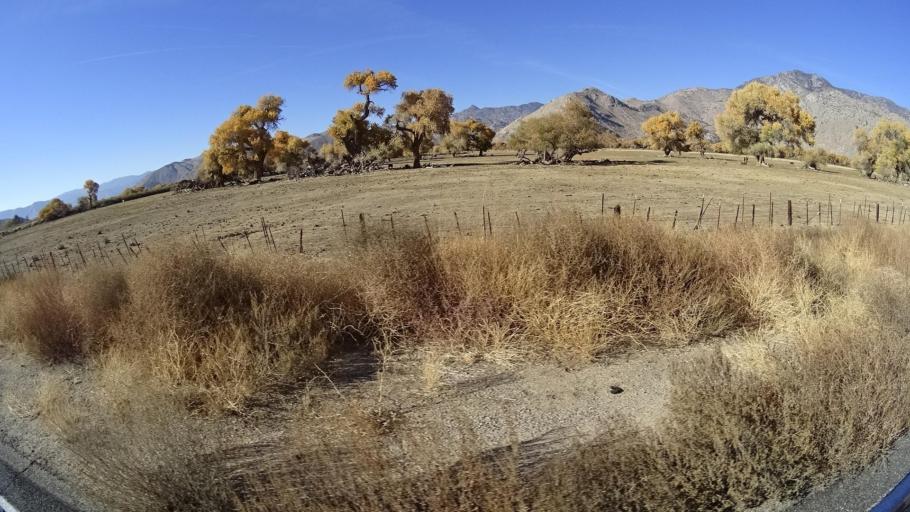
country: US
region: California
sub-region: Kern County
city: Weldon
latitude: 35.6720
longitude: -118.2605
